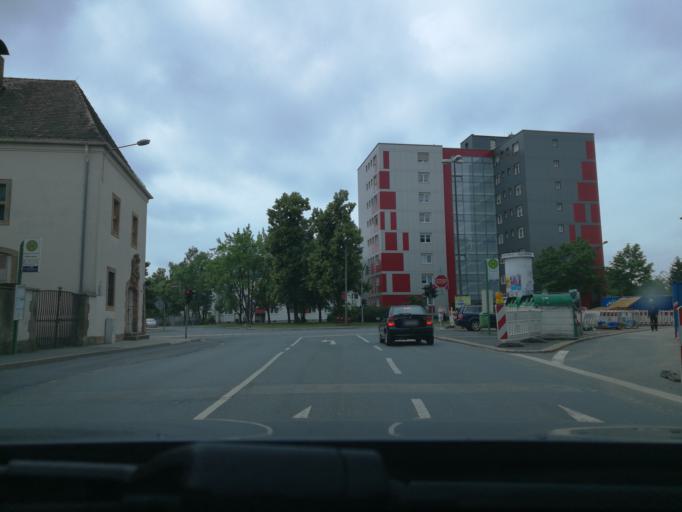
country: DE
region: Bavaria
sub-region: Regierungsbezirk Mittelfranken
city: Furth
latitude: 49.4786
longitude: 10.9702
